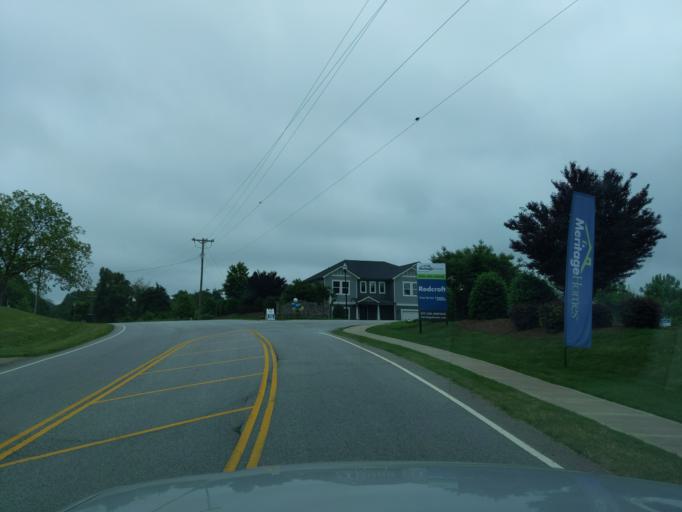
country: US
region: South Carolina
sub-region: Greenville County
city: Five Forks
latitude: 34.8519
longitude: -82.1975
